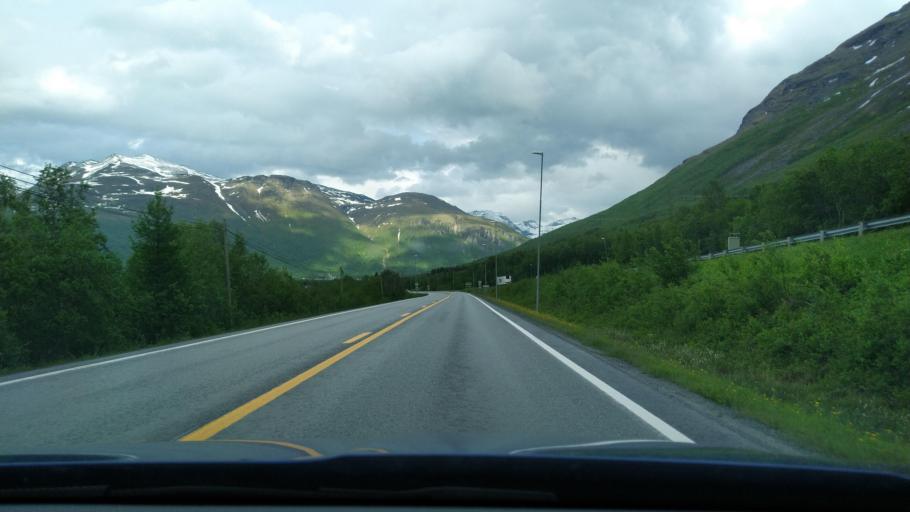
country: NO
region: Troms
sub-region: Balsfjord
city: Storsteinnes
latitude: 69.2134
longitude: 19.5283
